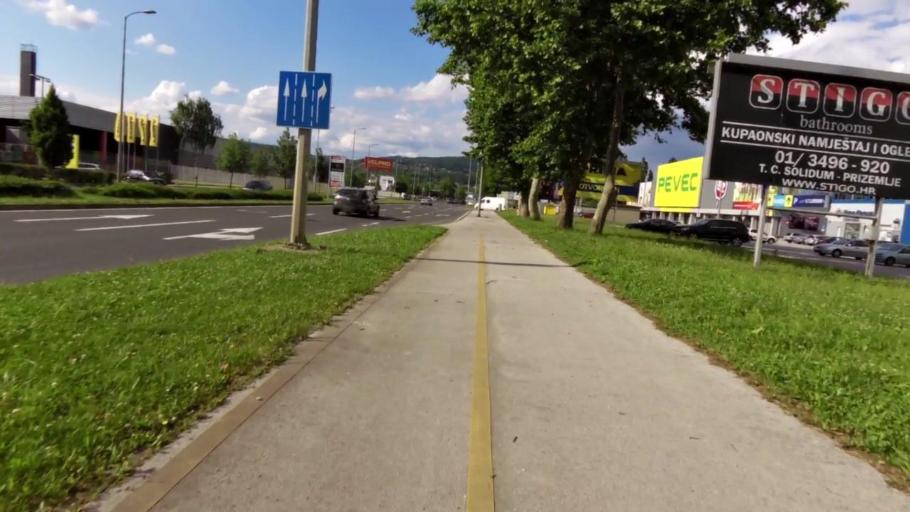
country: HR
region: Grad Zagreb
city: Jezdovec
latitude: 45.8042
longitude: 15.8584
